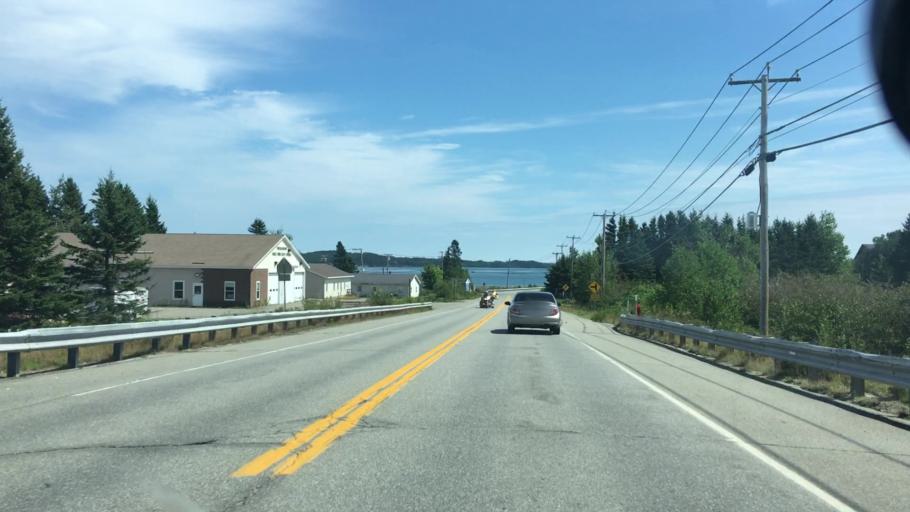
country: US
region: Maine
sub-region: Washington County
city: Eastport
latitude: 44.9559
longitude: -67.0443
